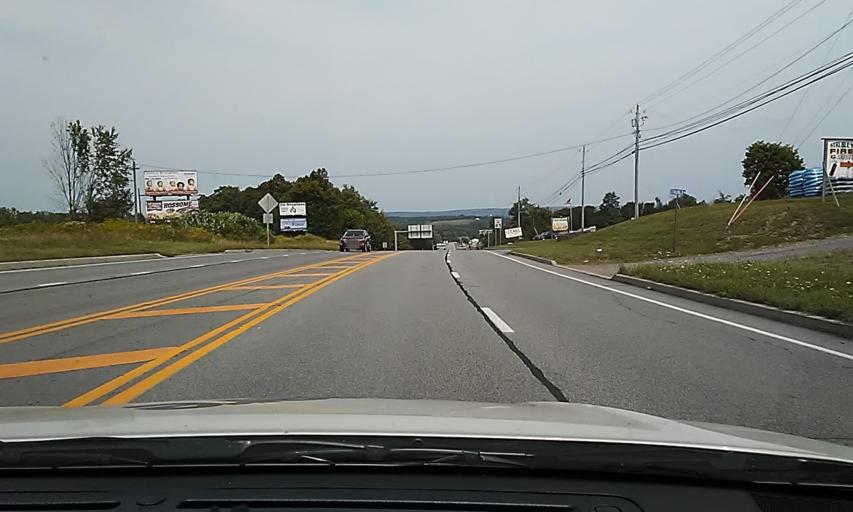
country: US
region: Pennsylvania
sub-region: Elk County
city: Saint Marys
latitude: 41.3679
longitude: -78.5571
